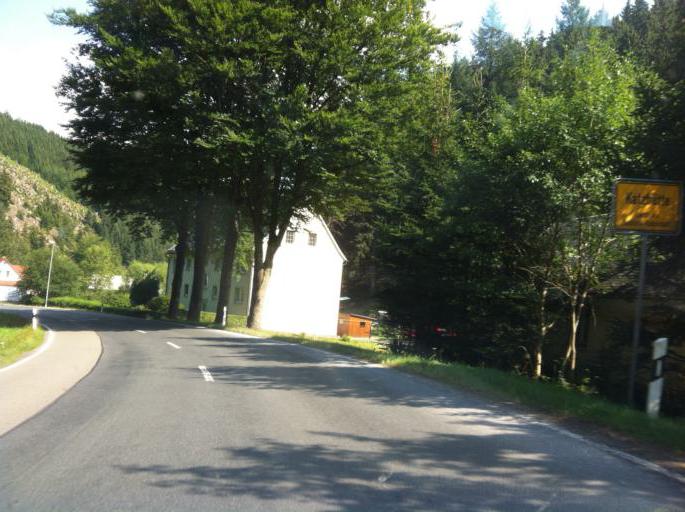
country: DE
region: Thuringia
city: Grossbreitenbach
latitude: 50.5530
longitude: 11.0141
